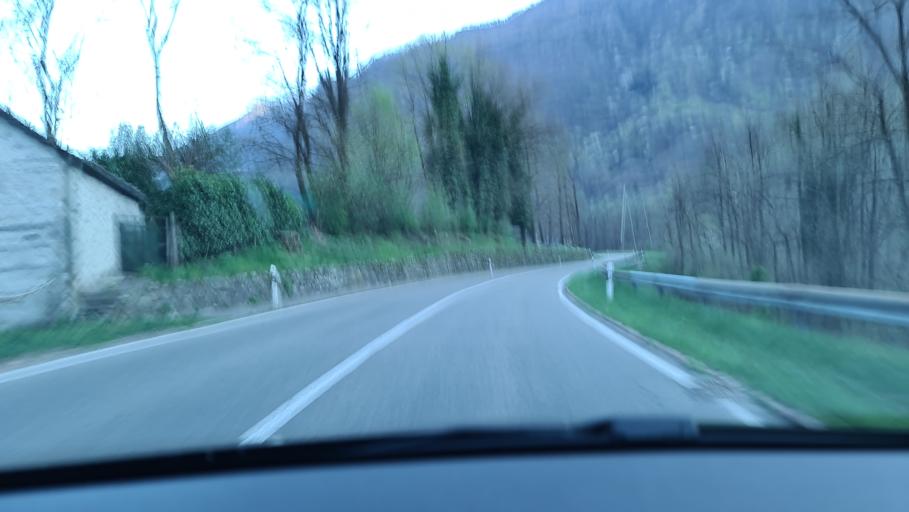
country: CH
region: Ticino
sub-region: Locarno District
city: Verscio
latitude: 46.2518
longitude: 8.6994
